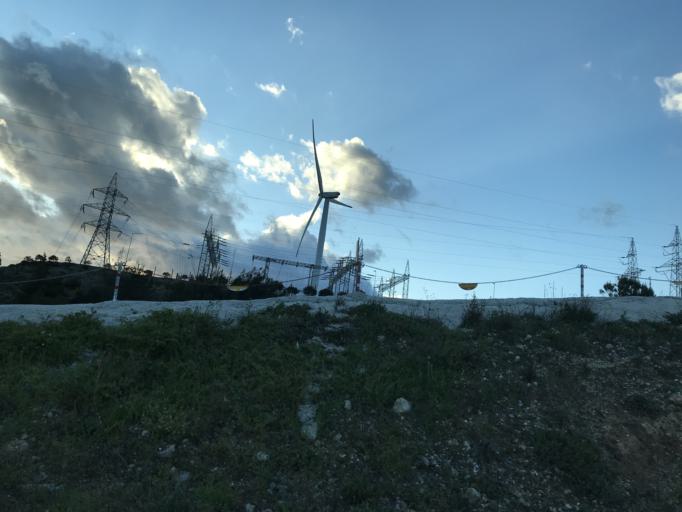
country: TR
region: Hatay
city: Buyukcat
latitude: 36.1043
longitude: 36.0437
